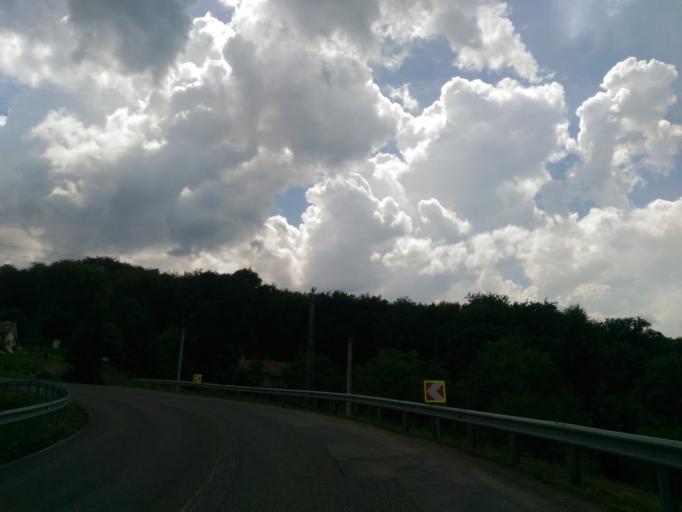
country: HU
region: Baranya
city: Komlo
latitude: 46.1582
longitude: 18.2383
